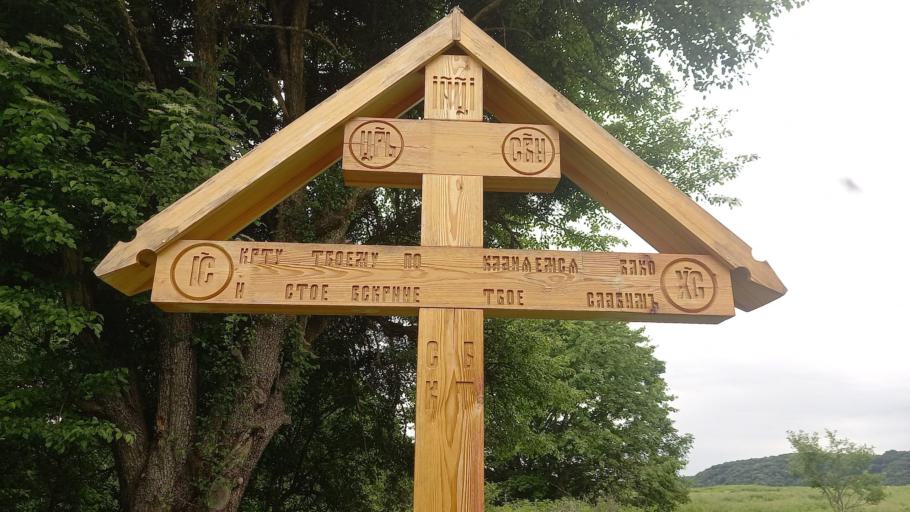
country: RU
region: Krasnodarskiy
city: Peredovaya
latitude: 44.0439
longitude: 41.3329
